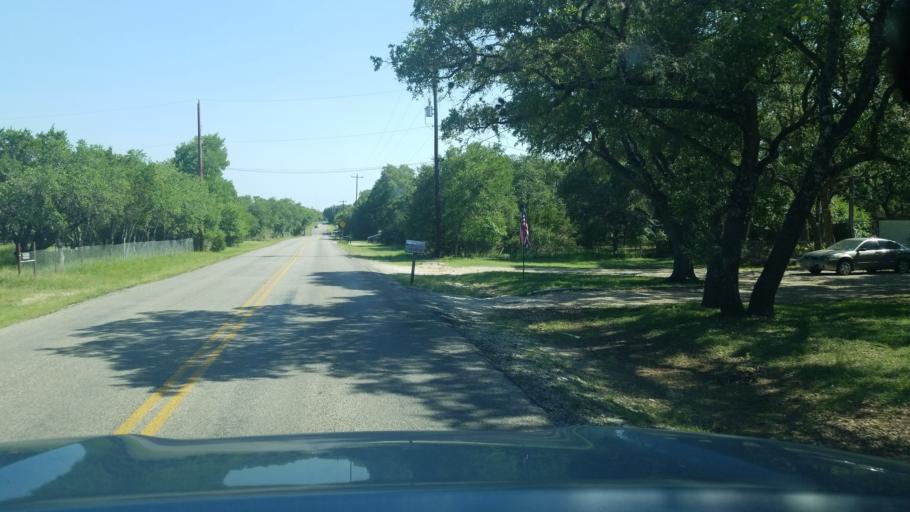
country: US
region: Texas
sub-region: Bexar County
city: Timberwood Park
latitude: 29.7503
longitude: -98.5128
